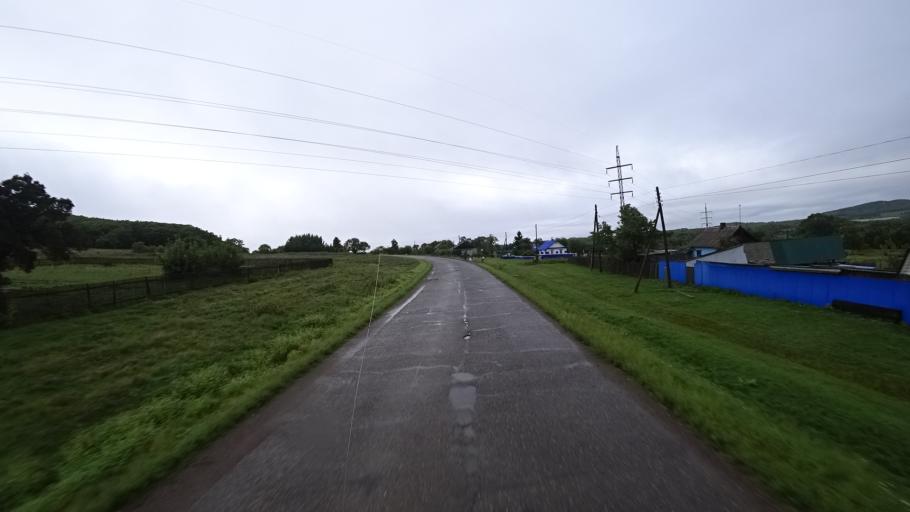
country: RU
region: Primorskiy
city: Monastyrishche
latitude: 44.2619
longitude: 132.4202
